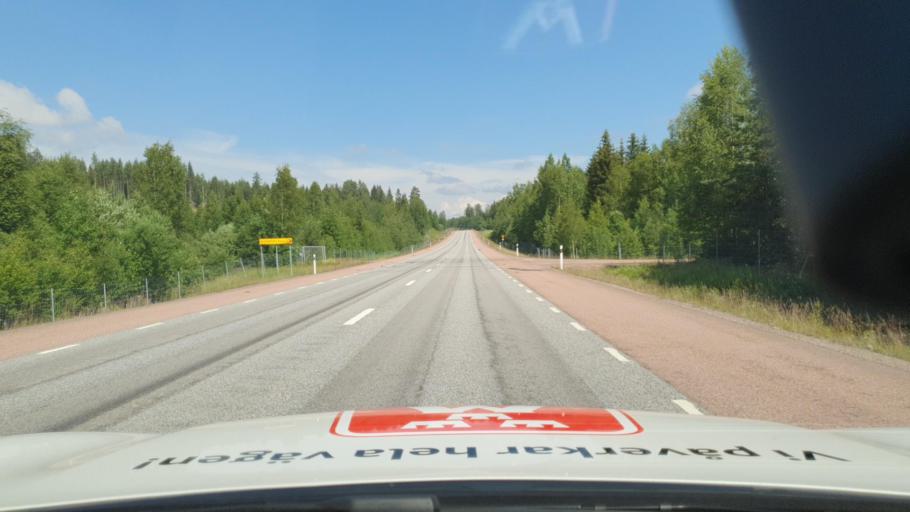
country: SE
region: Vaermland
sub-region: Torsby Kommun
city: Torsby
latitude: 60.1874
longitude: 13.0179
